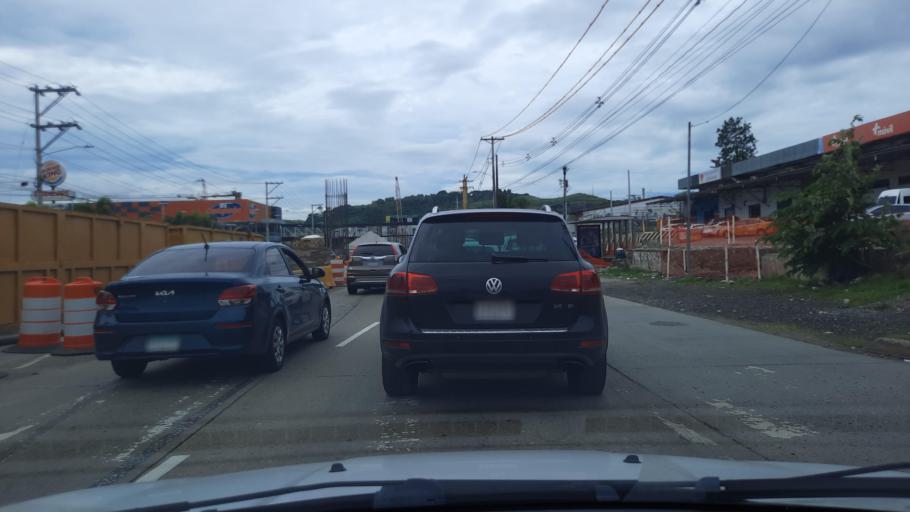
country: PA
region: Panama
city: Las Cumbres
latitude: 9.0746
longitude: -79.5248
